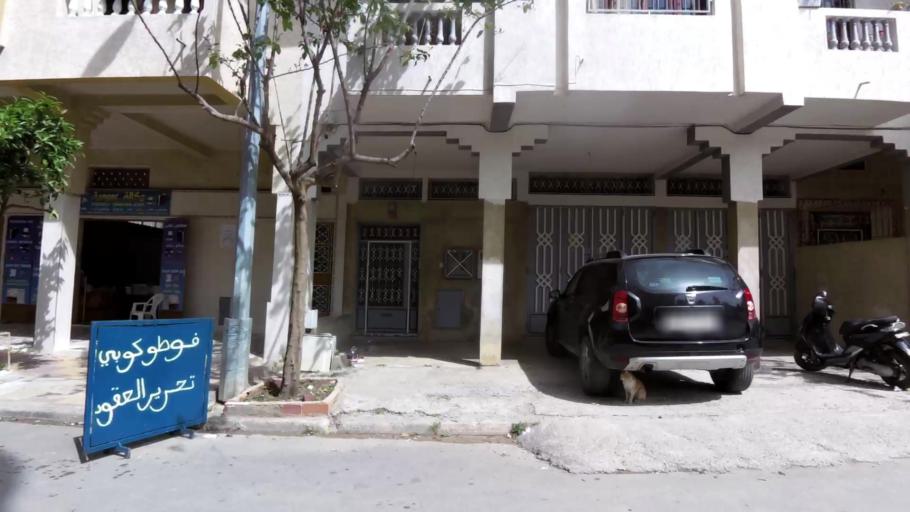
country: MA
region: Tanger-Tetouan
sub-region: Tanger-Assilah
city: Tangier
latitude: 35.7411
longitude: -5.8323
